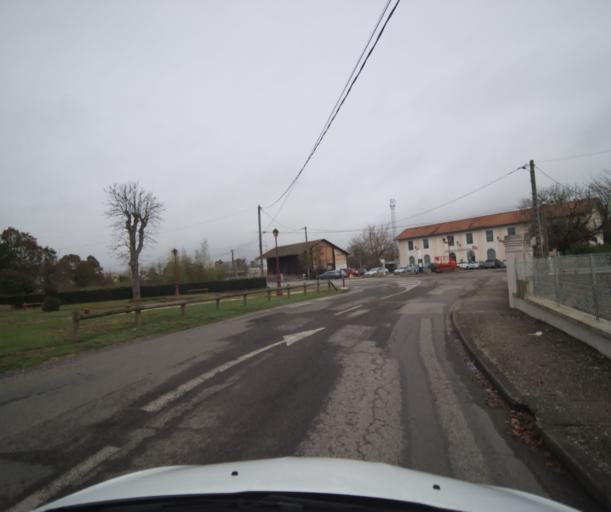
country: FR
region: Midi-Pyrenees
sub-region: Departement du Tarn-et-Garonne
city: Castelsarrasin
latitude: 44.0397
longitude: 1.1137
